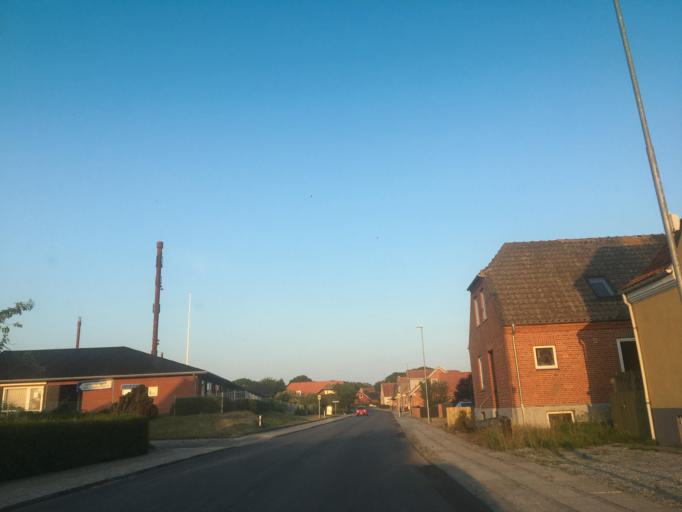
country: DK
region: North Denmark
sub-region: Thisted Kommune
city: Hurup
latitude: 56.7632
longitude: 8.3151
